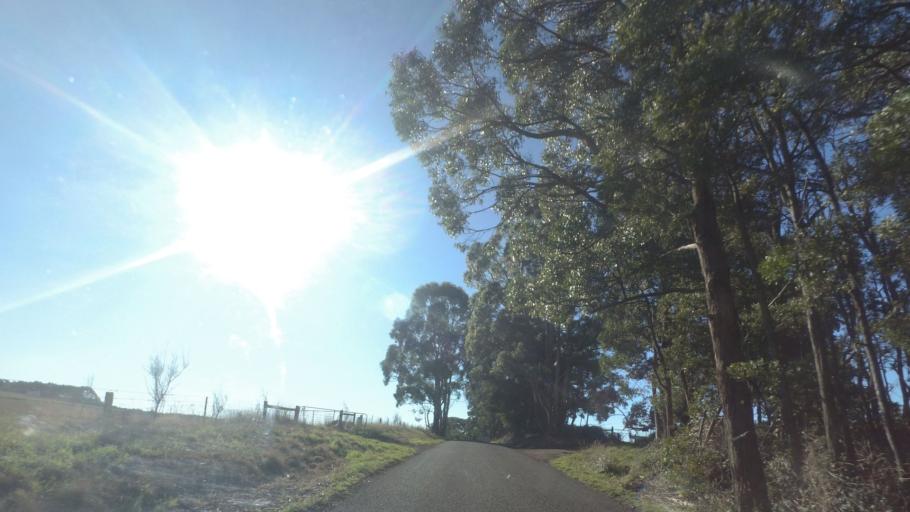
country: AU
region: Victoria
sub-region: Mount Alexander
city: Castlemaine
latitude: -37.3441
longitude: 144.3191
